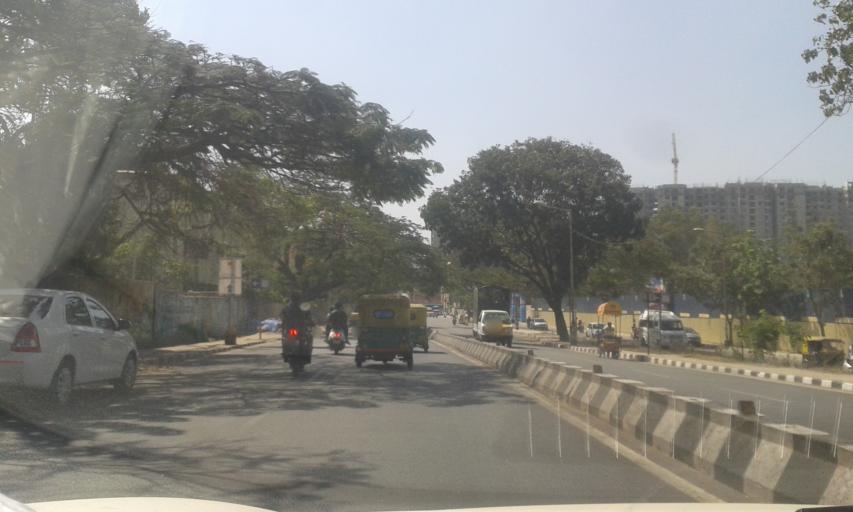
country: IN
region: Karnataka
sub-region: Bangalore Urban
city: Bangalore
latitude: 12.9812
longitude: 77.5644
